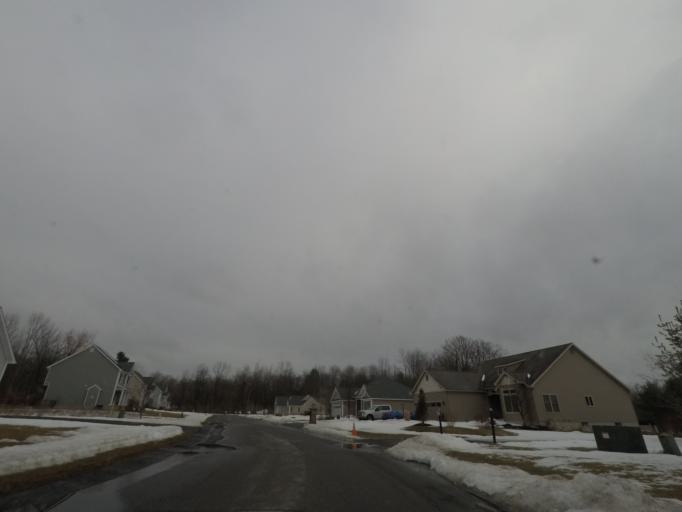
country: US
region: New York
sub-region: Schenectady County
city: Rotterdam
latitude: 42.7641
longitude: -73.9777
